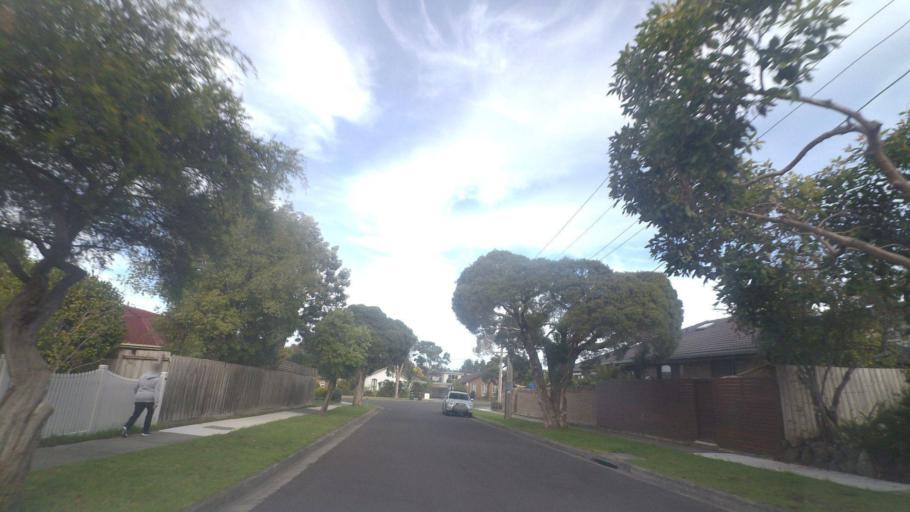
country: AU
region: Victoria
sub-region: Whitehorse
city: Vermont South
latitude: -37.8652
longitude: 145.1792
